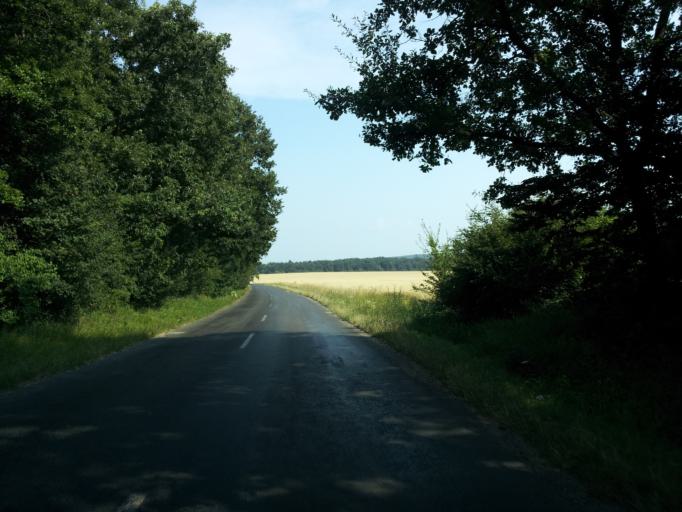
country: HU
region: Veszprem
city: Nemesvamos
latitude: 47.0253
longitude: 17.9019
